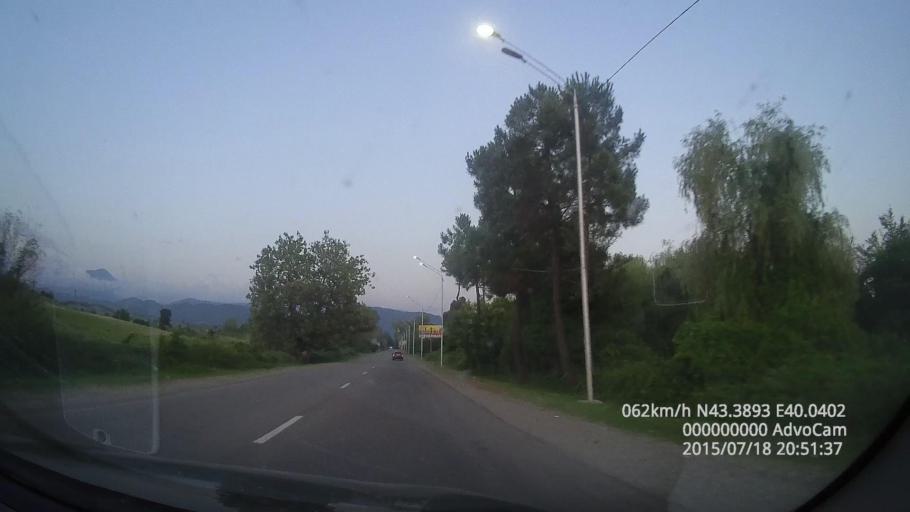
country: GE
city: Gantiadi
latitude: 43.3890
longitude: 40.0418
